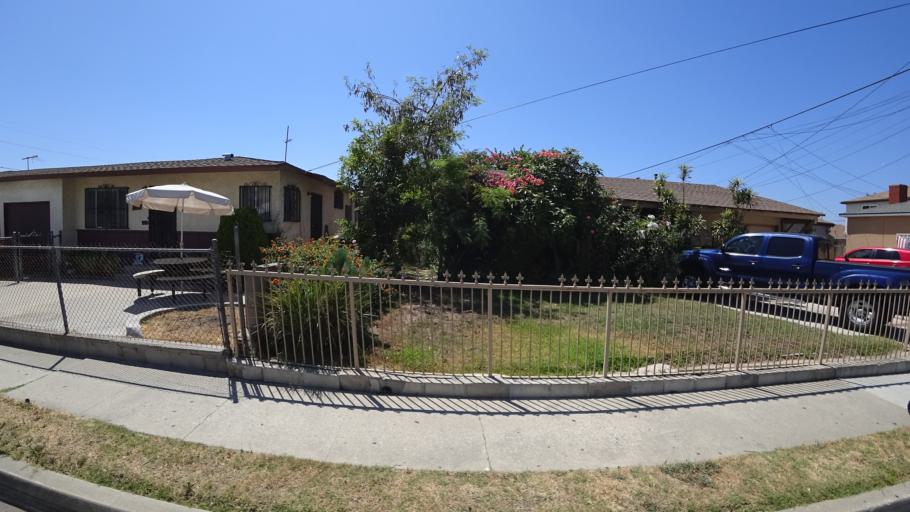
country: US
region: California
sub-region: Los Angeles County
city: Lennox
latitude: 33.9324
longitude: -118.3394
